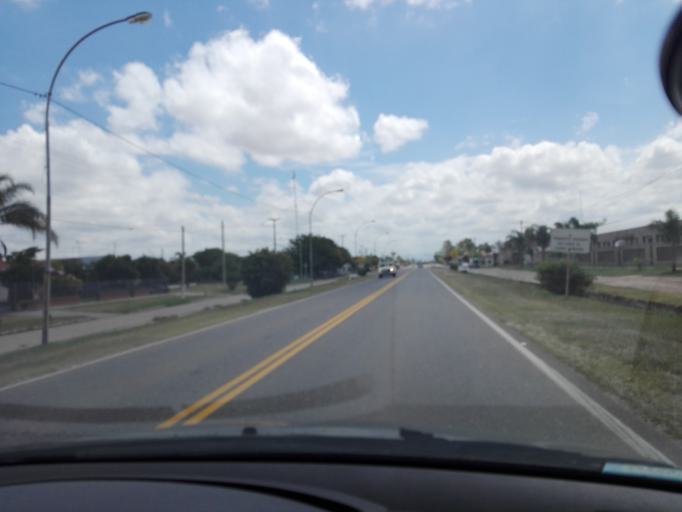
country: AR
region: Cordoba
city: Toledo
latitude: -31.6487
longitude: -64.0848
